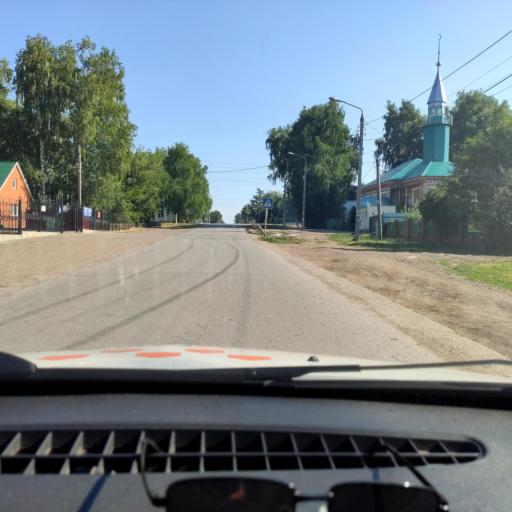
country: RU
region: Bashkortostan
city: Tolbazy
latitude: 54.0169
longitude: 55.8836
